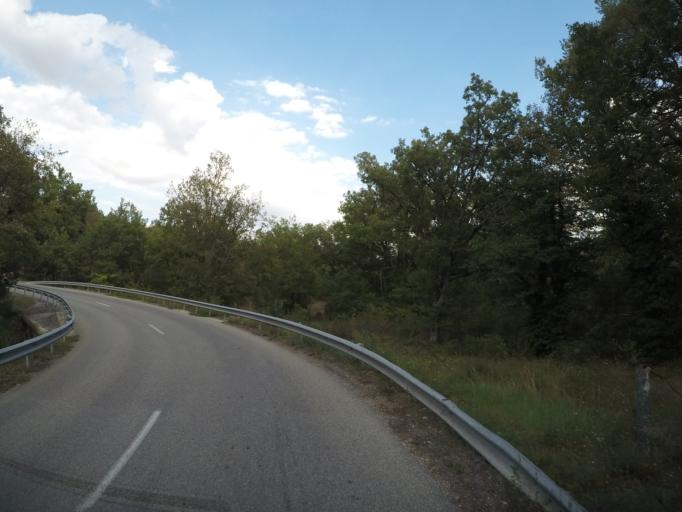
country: FR
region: Provence-Alpes-Cote d'Azur
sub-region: Departement des Alpes-de-Haute-Provence
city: Valensole
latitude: 43.8335
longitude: 6.0096
